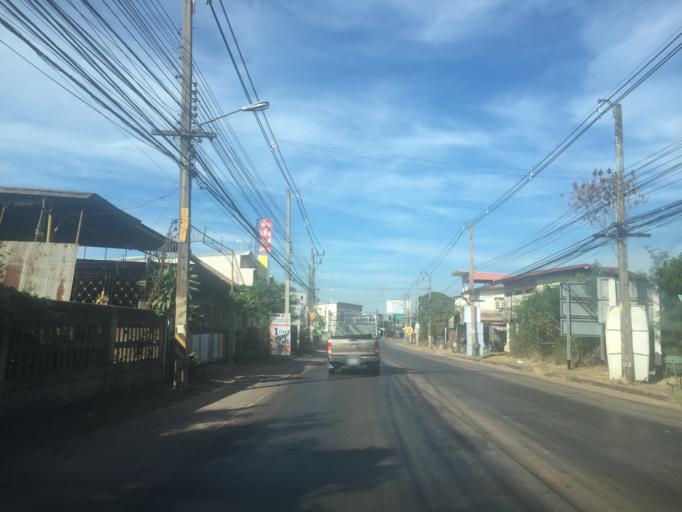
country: TH
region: Changwat Udon Thani
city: Kumphawapi
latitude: 17.1112
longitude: 103.0097
